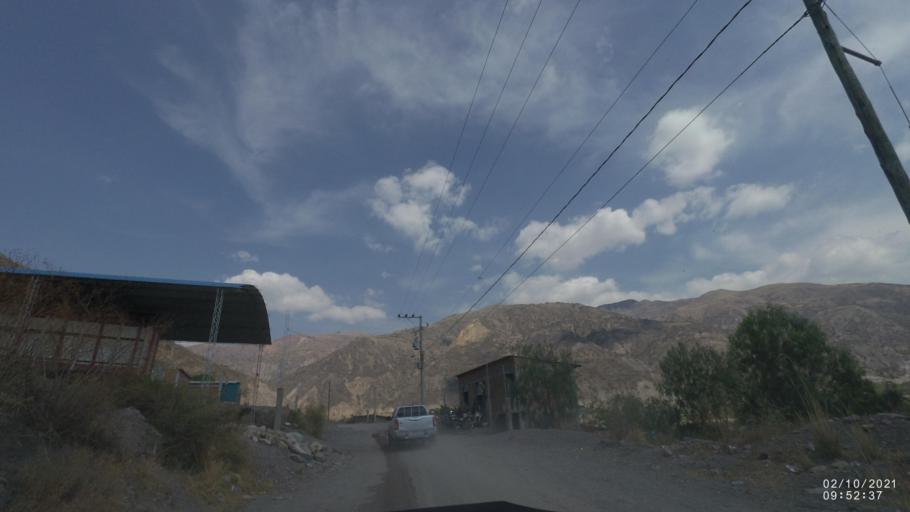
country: BO
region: Cochabamba
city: Irpa Irpa
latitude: -17.8005
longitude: -66.3450
